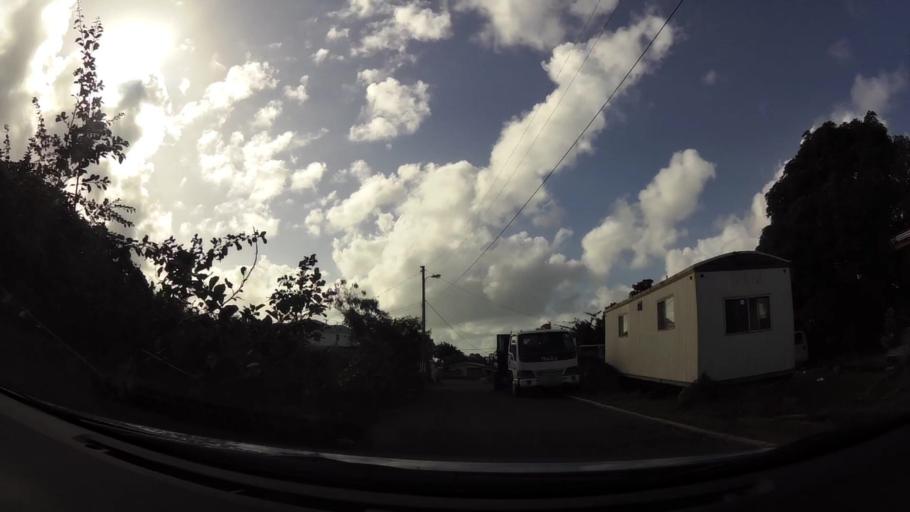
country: KN
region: Saint Paul Charlestown
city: Charlestown
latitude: 17.1396
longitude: -62.6262
